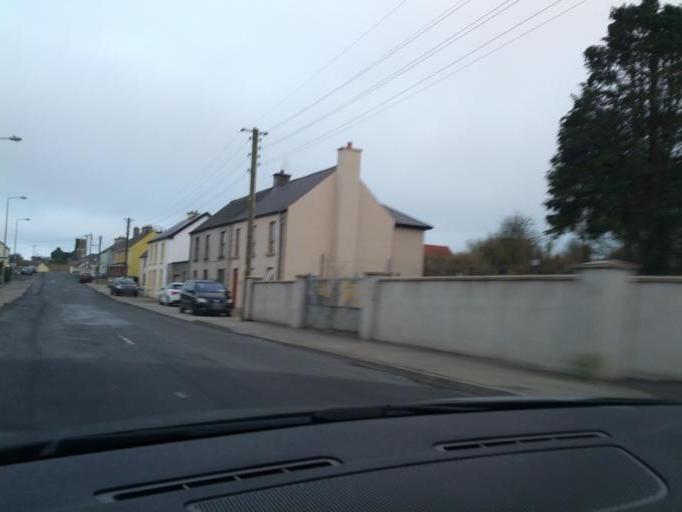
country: IE
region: Connaught
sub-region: Sligo
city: Ballymote
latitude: 53.9928
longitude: -8.5149
